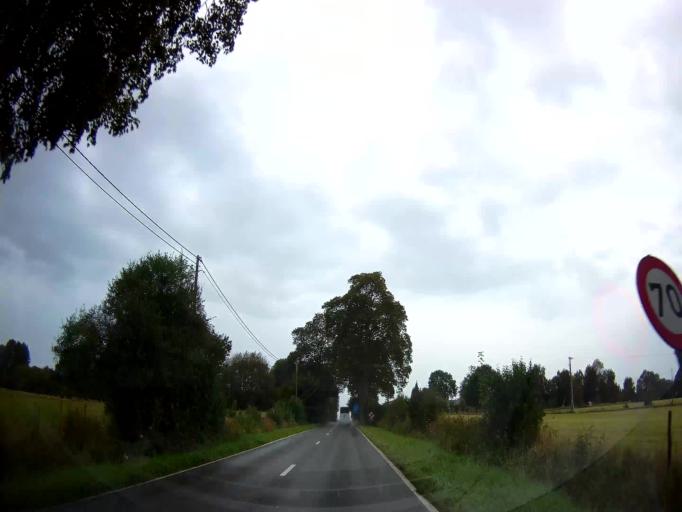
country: BE
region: Wallonia
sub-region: Province de Liege
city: Trooz
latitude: 50.5211
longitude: 5.7264
